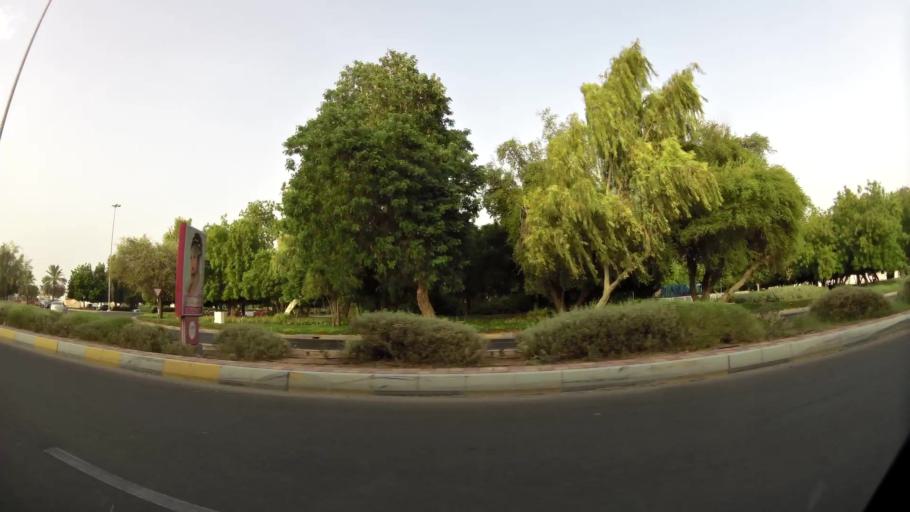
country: OM
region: Al Buraimi
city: Al Buraymi
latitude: 24.2464
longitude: 55.7394
